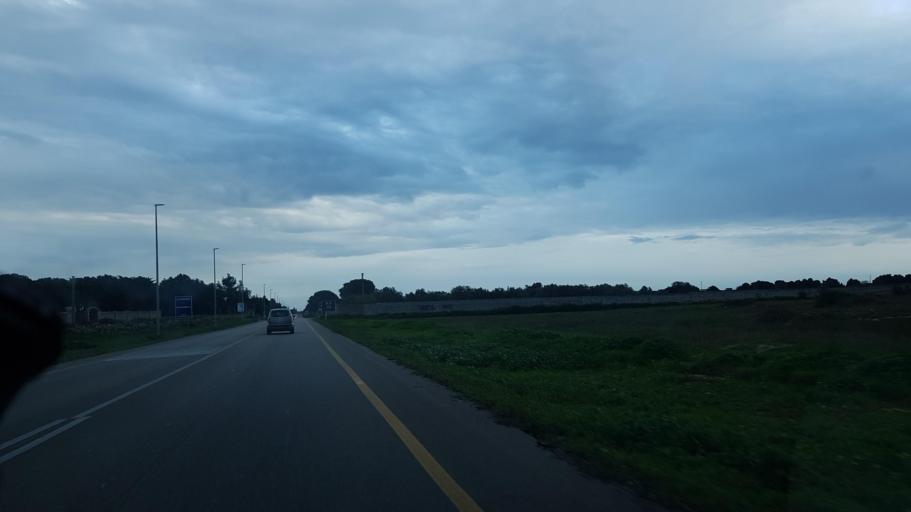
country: IT
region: Apulia
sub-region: Provincia di Lecce
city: Merine
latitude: 40.3434
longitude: 18.2082
